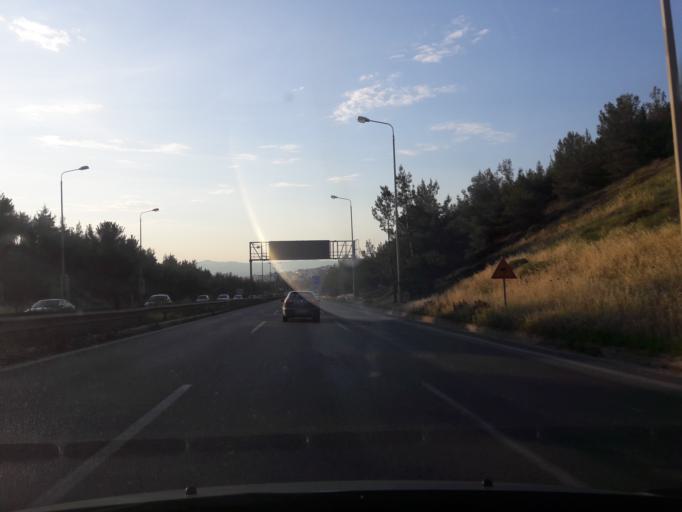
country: GR
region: Central Macedonia
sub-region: Nomos Thessalonikis
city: Agios Pavlos
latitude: 40.6467
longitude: 22.9683
